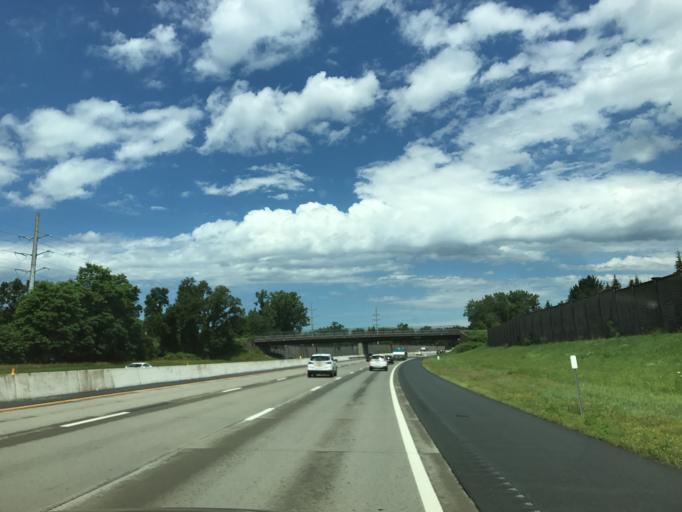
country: US
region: New York
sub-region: Albany County
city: McKownville
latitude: 42.6758
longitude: -73.8440
